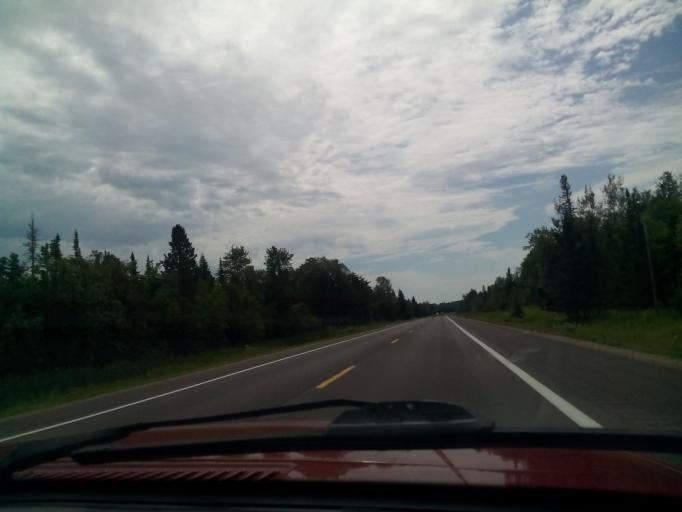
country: US
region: Michigan
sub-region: Schoolcraft County
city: Manistique
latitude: 46.0694
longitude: -85.9584
